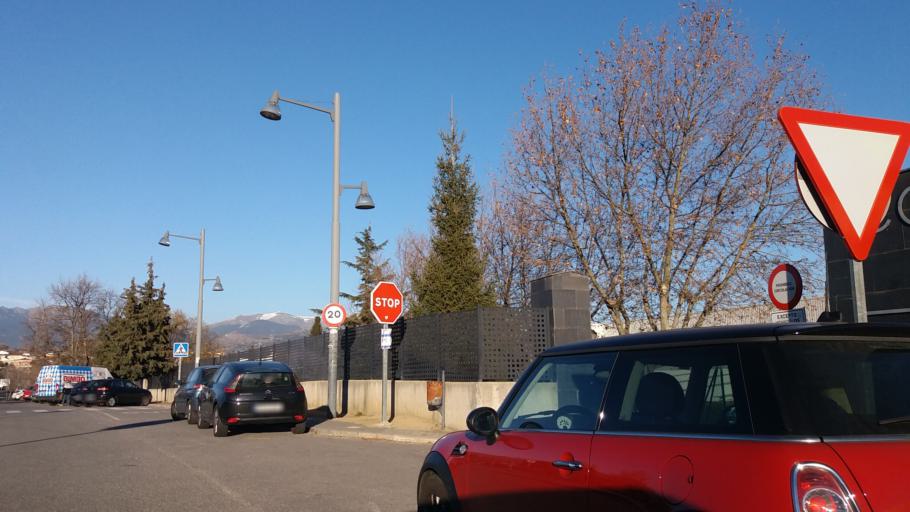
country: ES
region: Madrid
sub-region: Provincia de Madrid
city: Guadarrama
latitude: 40.6644
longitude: -4.0898
